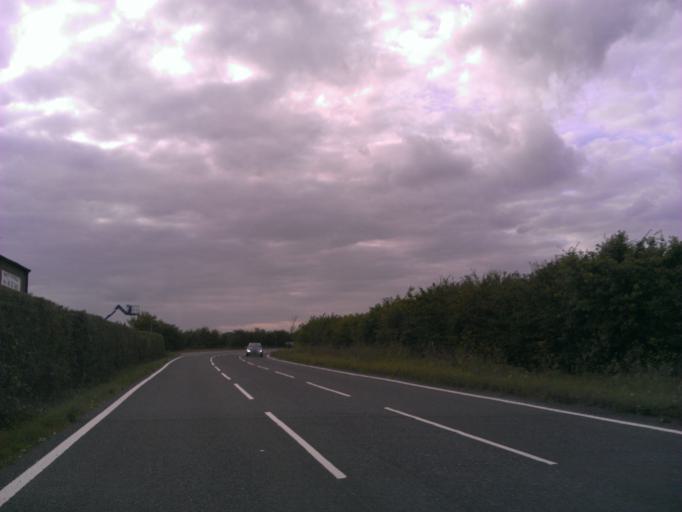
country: GB
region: England
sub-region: Essex
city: Wivenhoe
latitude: 51.8697
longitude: 0.9805
